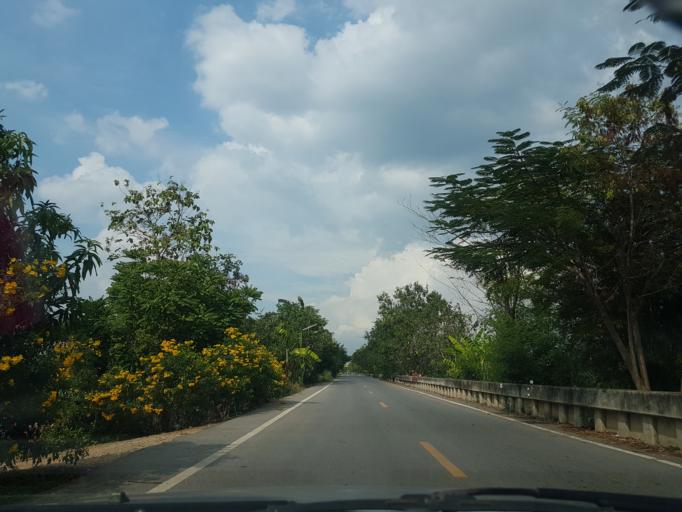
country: TH
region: Sara Buri
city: Nong Khae
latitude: 14.2405
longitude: 100.8914
